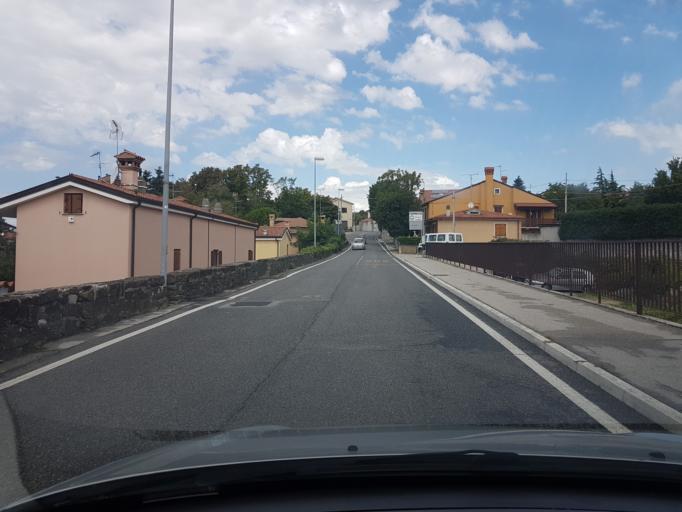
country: IT
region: Friuli Venezia Giulia
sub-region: Provincia di Trieste
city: Prosecco-Contovello
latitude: 45.7046
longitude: 13.7327
